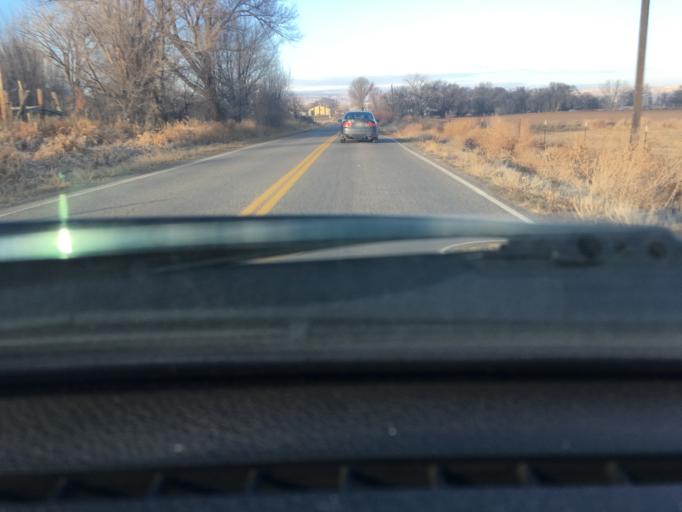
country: US
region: Colorado
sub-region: Delta County
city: Delta
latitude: 38.7410
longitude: -108.0961
